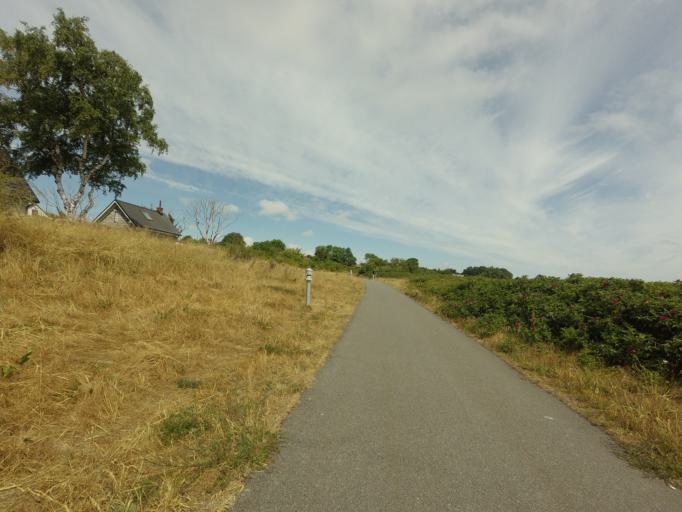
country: SE
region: Skane
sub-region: Simrishamns Kommun
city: Simrishamn
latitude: 55.5231
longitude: 14.3475
